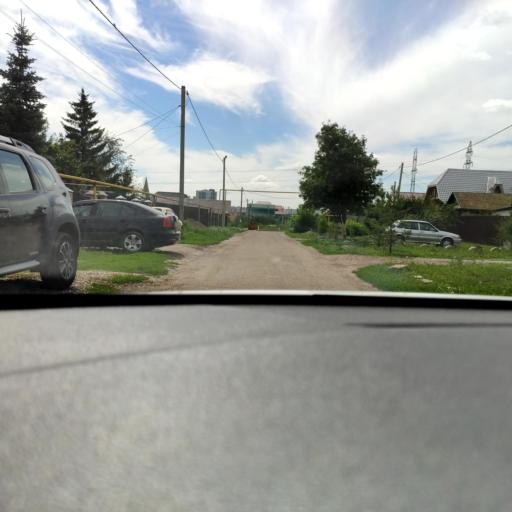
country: RU
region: Tatarstan
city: Vysokaya Gora
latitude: 55.8047
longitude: 49.2566
